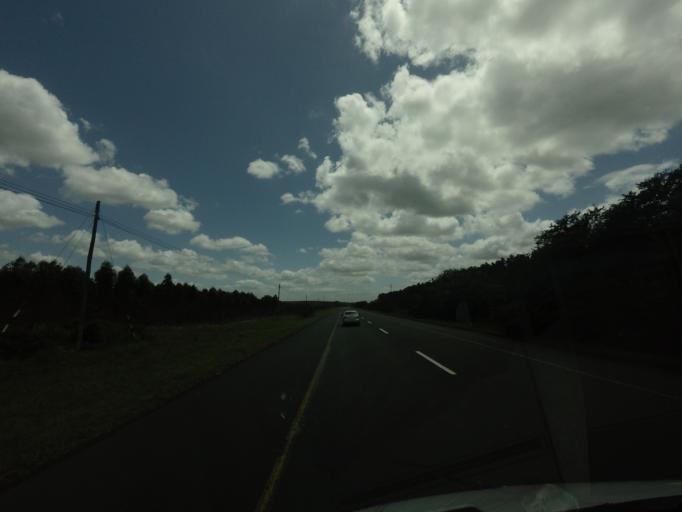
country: ZA
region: KwaZulu-Natal
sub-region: uThungulu District Municipality
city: KwaMbonambi
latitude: -28.5571
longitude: 32.1171
